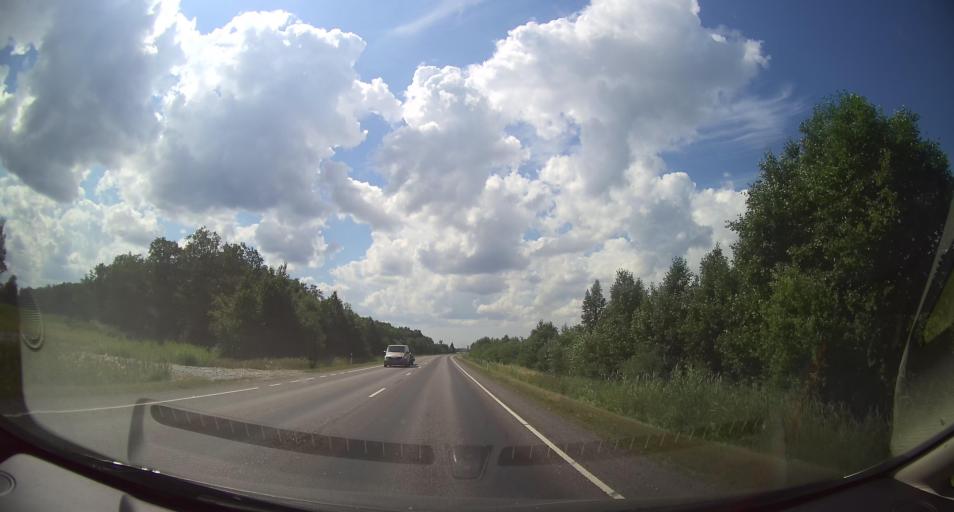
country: EE
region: Laeaene
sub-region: Lihula vald
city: Lihula
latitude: 58.6909
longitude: 23.8176
